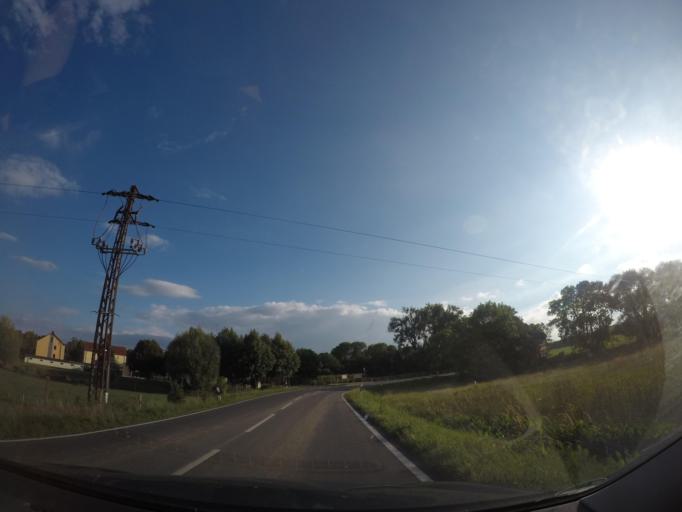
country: DE
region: Saxony-Anhalt
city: Weferlingen
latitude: 52.3489
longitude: 11.0774
